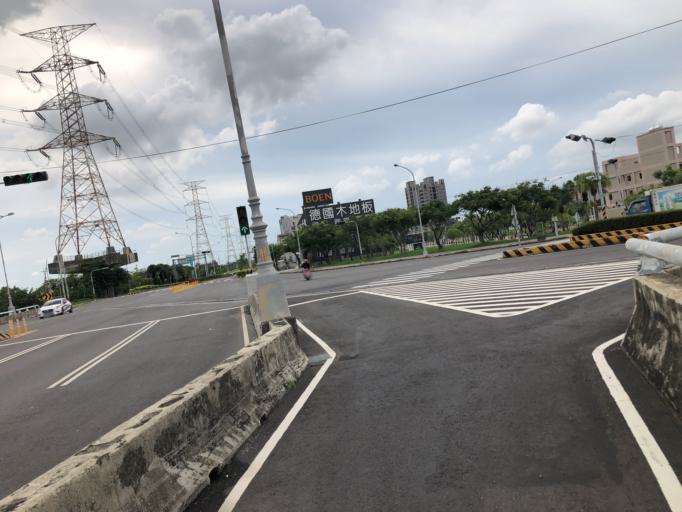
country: TW
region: Taiwan
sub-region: Changhua
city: Chang-hua
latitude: 24.1031
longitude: 120.6113
